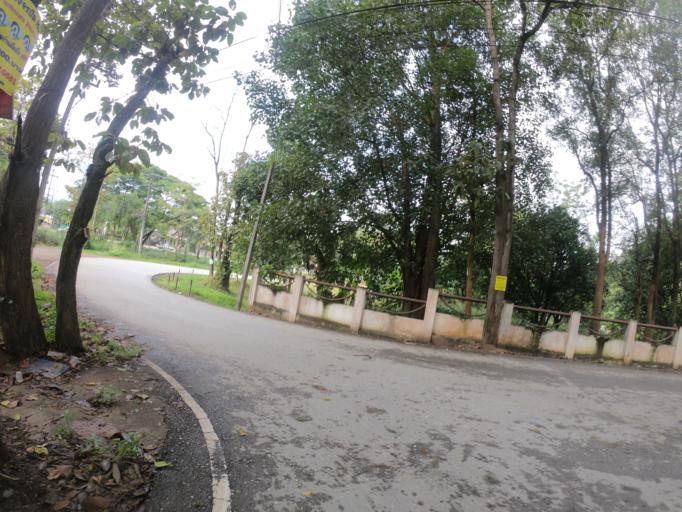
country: TH
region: Chiang Mai
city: Chiang Mai
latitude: 18.8202
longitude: 98.9734
